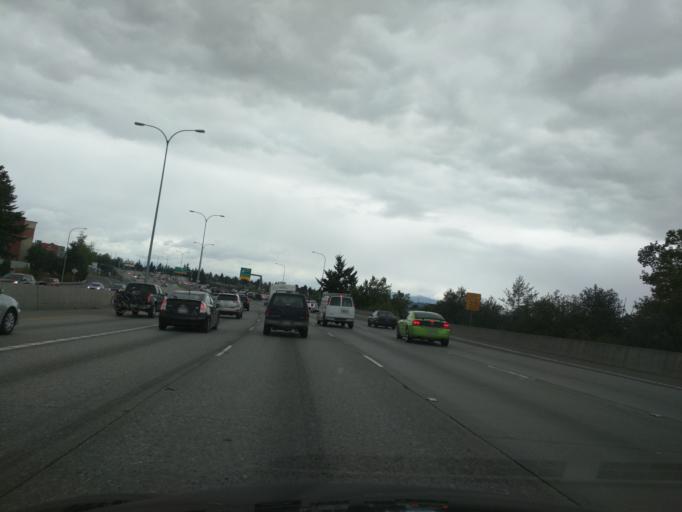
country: US
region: Washington
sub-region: Snohomish County
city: Everett
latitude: 47.9727
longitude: -122.1921
